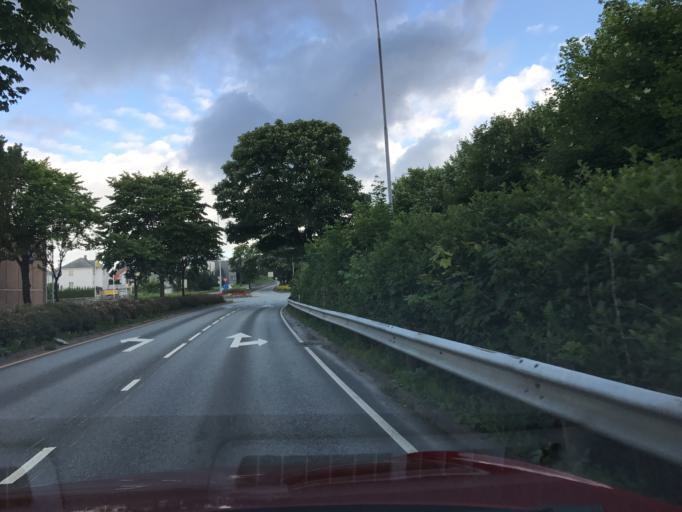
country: NO
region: Rogaland
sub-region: Haugesund
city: Haugesund
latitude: 59.4165
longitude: 5.2727
